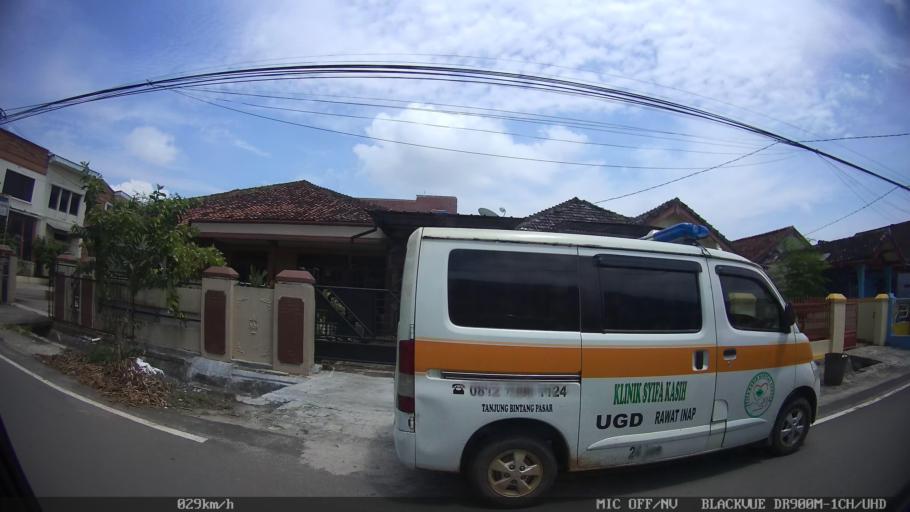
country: ID
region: Lampung
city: Kedaton
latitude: -5.3685
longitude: 105.3031
